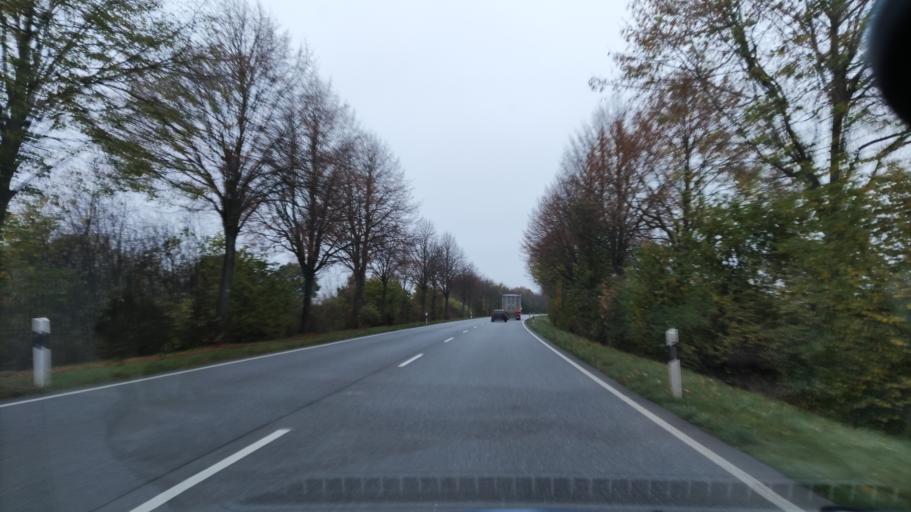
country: DE
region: Schleswig-Holstein
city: Fredeburg
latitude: 53.6832
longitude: 10.7290
